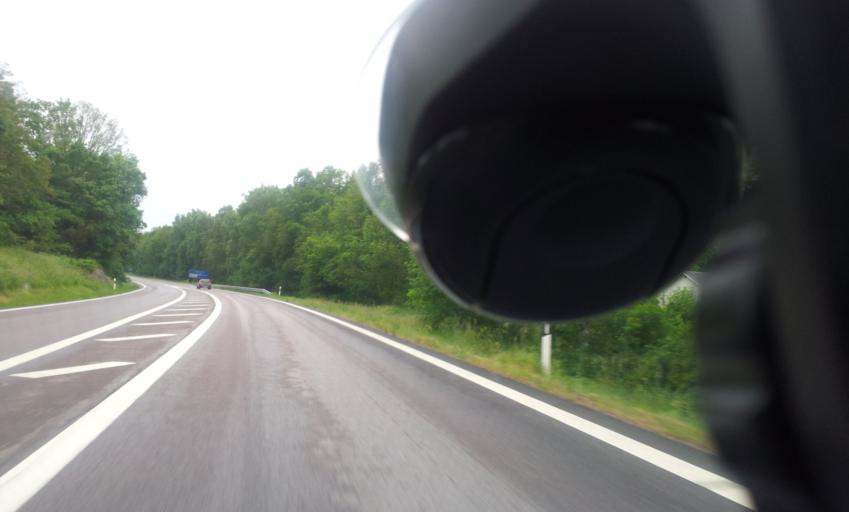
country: SE
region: Kalmar
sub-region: Monsteras Kommun
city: Moensteras
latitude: 57.0573
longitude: 16.4410
